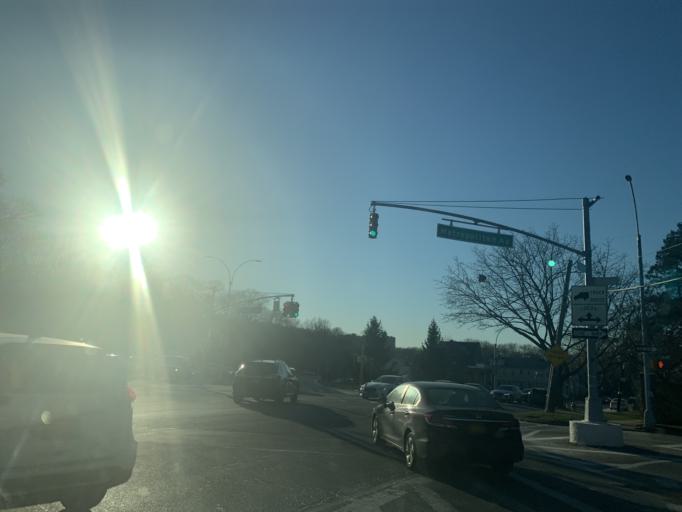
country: US
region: New York
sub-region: Queens County
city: Borough of Queens
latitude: 40.7094
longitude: -73.8430
